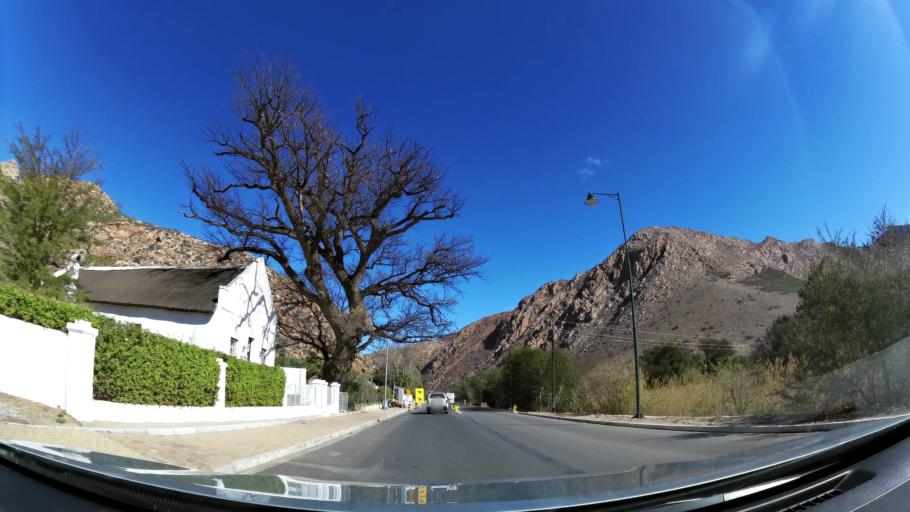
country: ZA
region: Western Cape
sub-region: Cape Winelands District Municipality
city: Ashton
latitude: -33.7919
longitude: 20.1095
